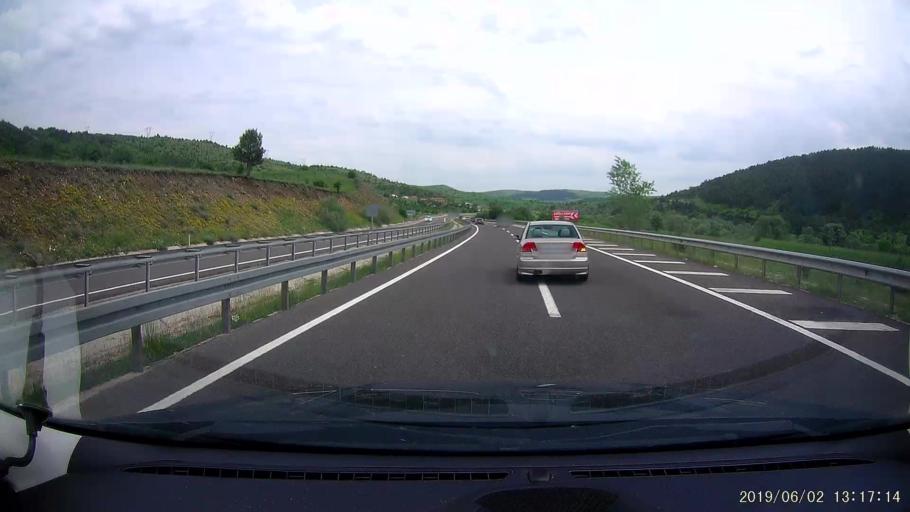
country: TR
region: Karabuk
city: Gozyeri
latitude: 40.8410
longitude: 32.6979
